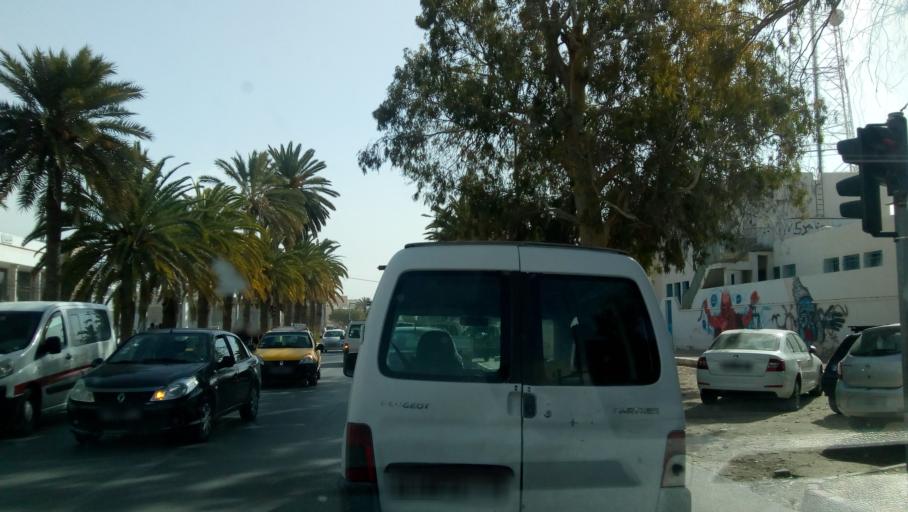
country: TN
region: Qabis
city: Gabes
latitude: 33.8849
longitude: 10.0917
